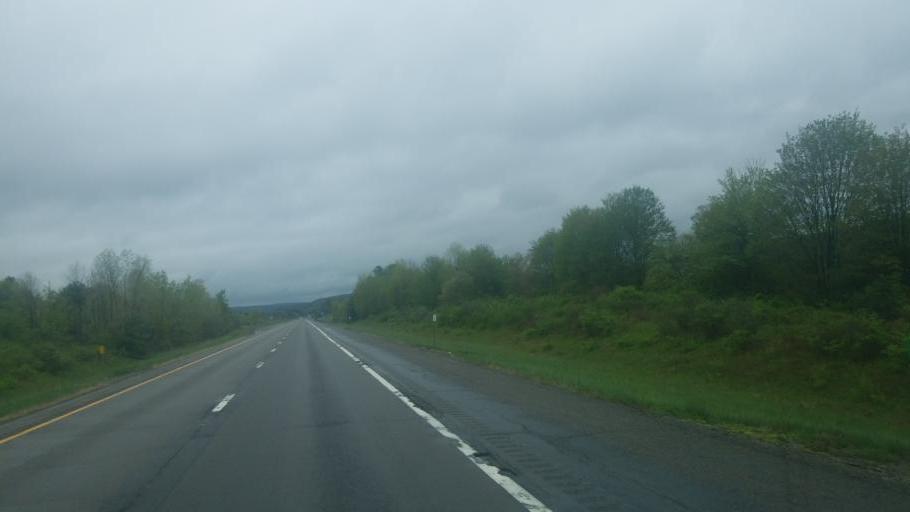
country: US
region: New York
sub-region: Allegany County
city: Belmont
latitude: 42.2966
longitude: -77.9954
